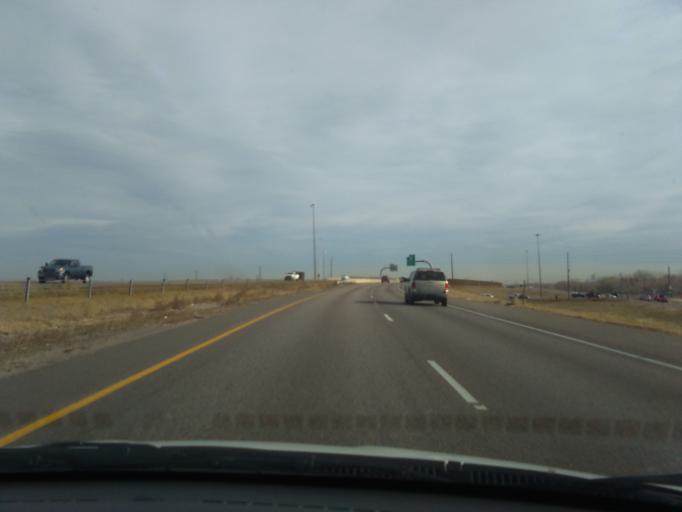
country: US
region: Colorado
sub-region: Adams County
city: Berkley
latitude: 39.7952
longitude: -105.0562
